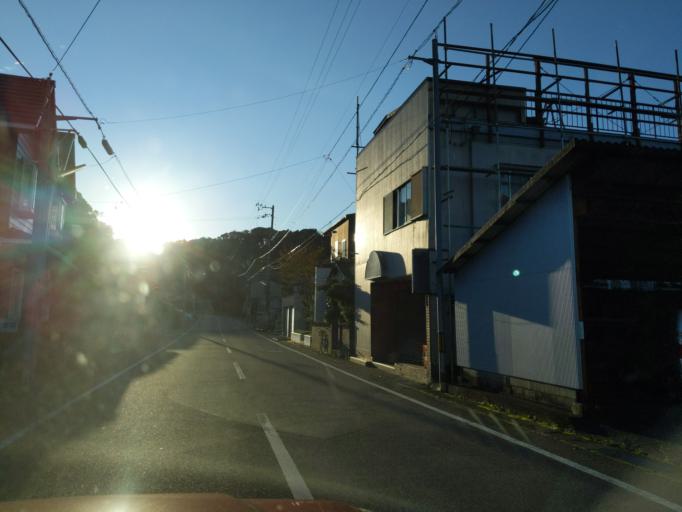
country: JP
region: Kochi
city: Muroto-misakicho
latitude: 33.5440
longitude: 134.2968
